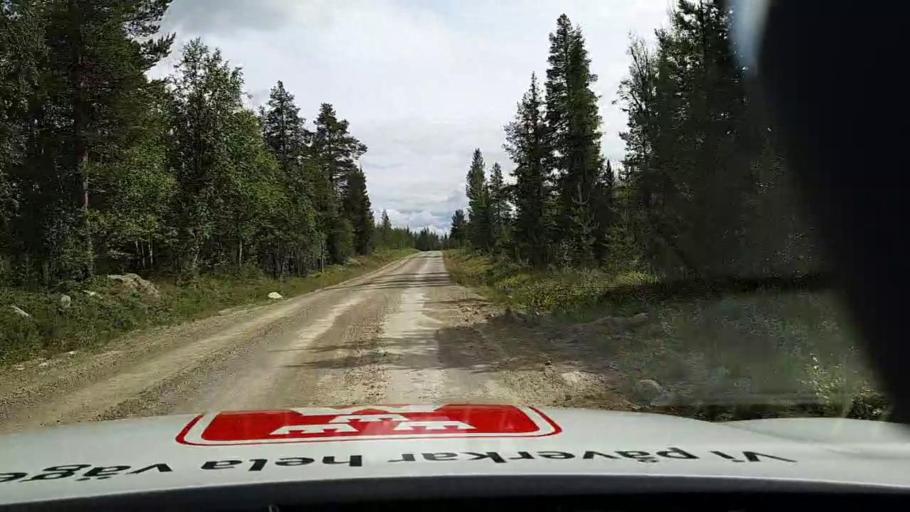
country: SE
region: Jaemtland
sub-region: Are Kommun
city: Jarpen
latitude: 62.5388
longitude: 13.4752
